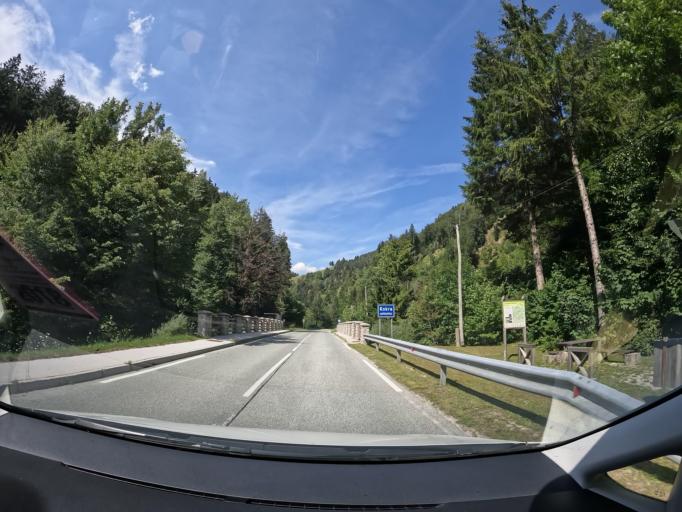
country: SI
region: Preddvor
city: Preddvor
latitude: 46.3717
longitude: 14.4067
